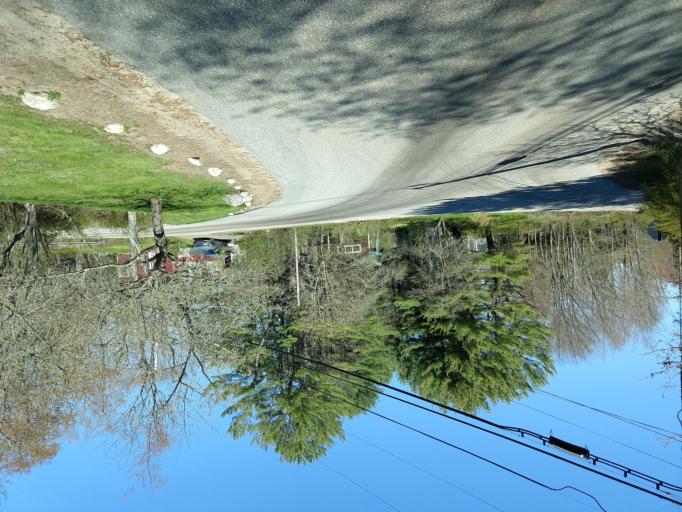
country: US
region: Maine
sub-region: York County
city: Arundel
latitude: 43.3964
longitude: -70.4515
